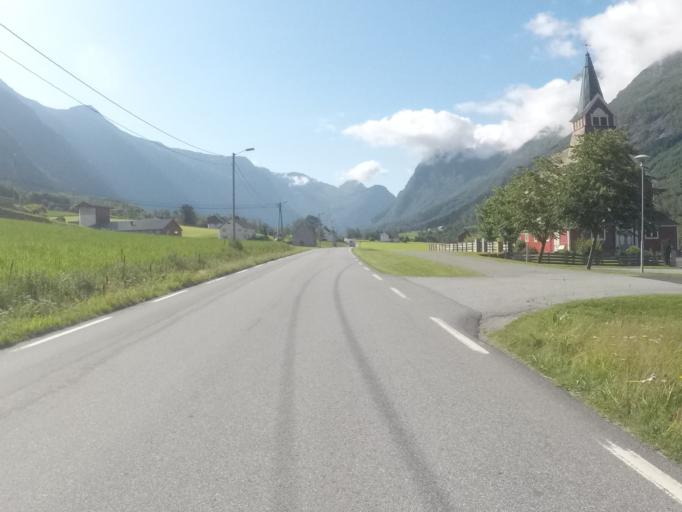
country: NO
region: Sogn og Fjordane
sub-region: Stryn
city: Stryn
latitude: 61.8281
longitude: 6.8086
